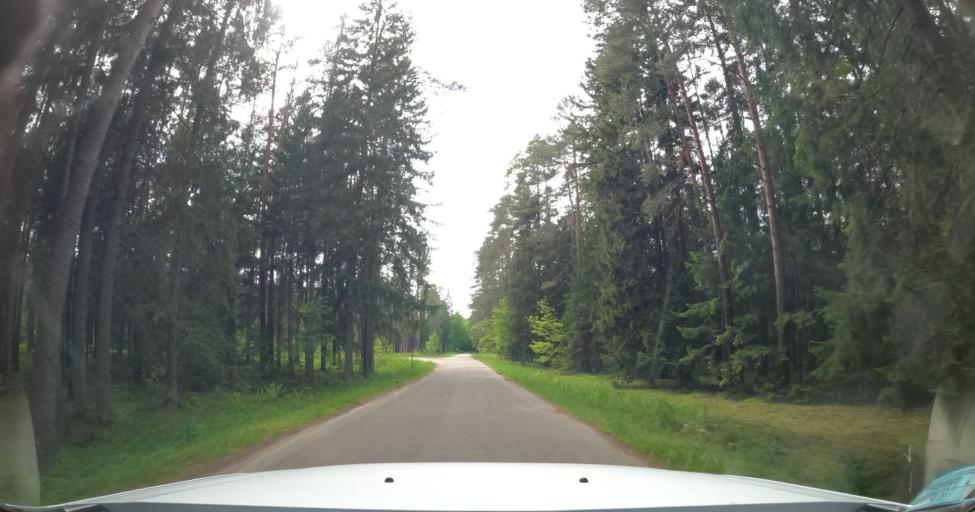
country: PL
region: Warmian-Masurian Voivodeship
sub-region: Powiat lidzbarski
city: Lubomino
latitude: 54.1047
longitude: 20.3576
